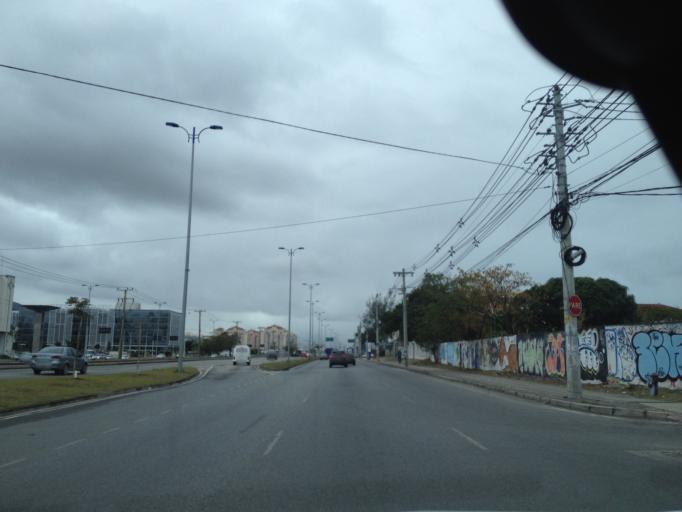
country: BR
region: Rio de Janeiro
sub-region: Nilopolis
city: Nilopolis
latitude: -23.0184
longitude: -43.4813
